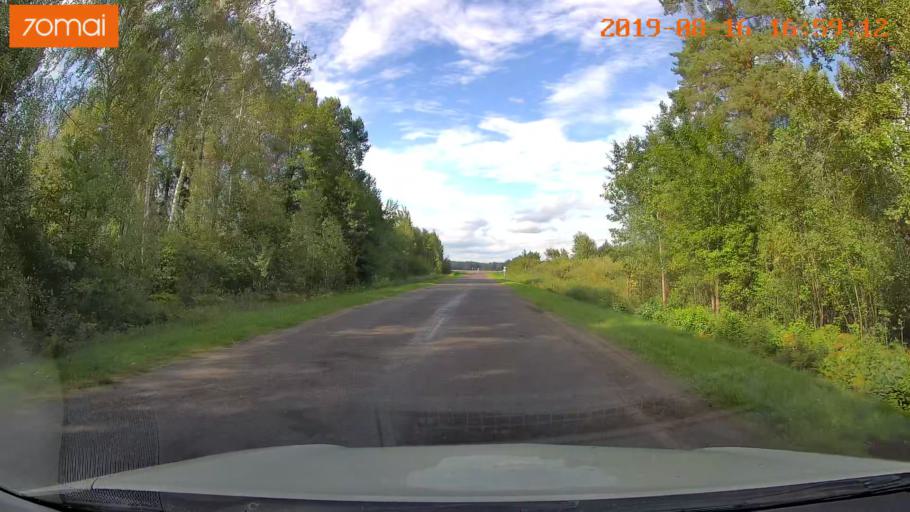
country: BY
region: Mogilev
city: Hlusha
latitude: 53.2795
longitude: 28.8401
